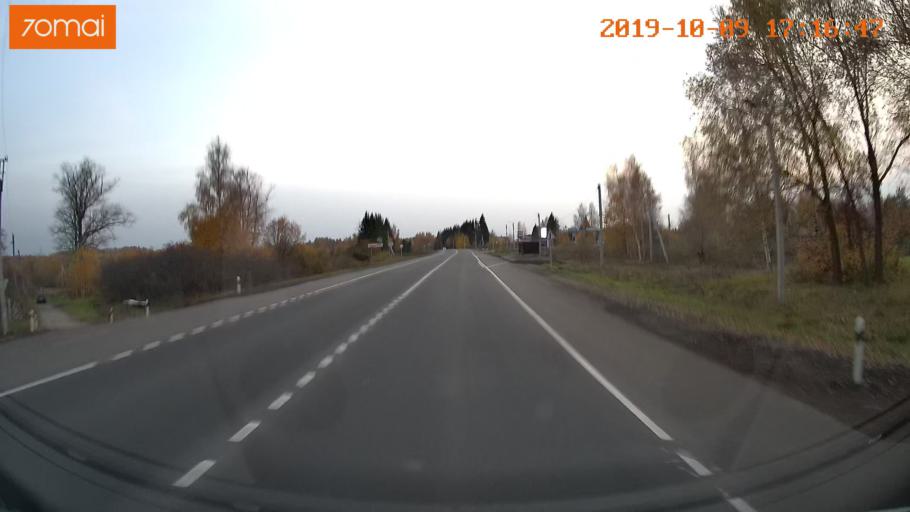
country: RU
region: Ivanovo
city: Furmanov
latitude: 57.2845
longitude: 41.1613
